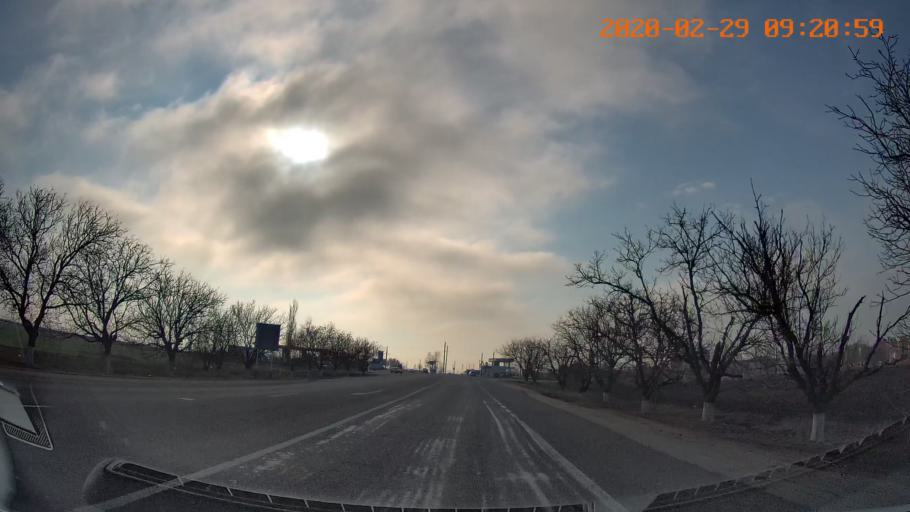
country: MD
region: Telenesti
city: Pervomaisc
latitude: 46.7416
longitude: 29.9541
